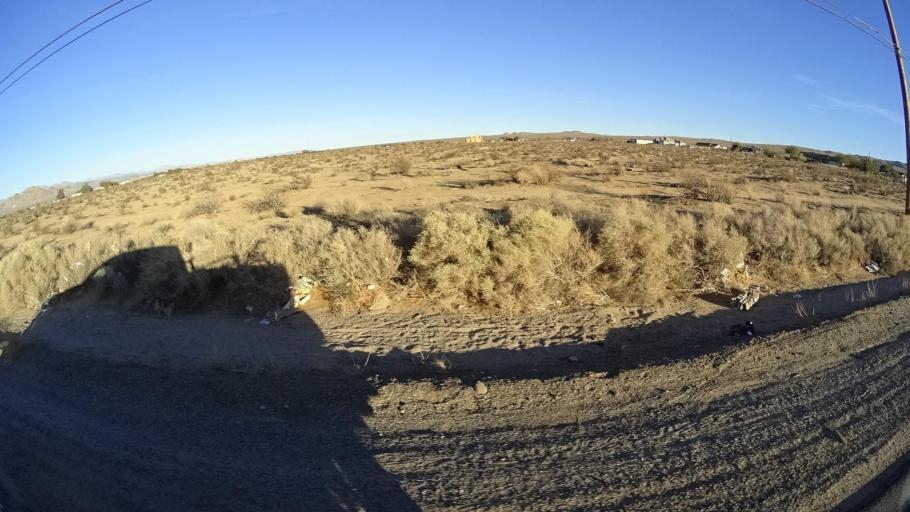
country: US
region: California
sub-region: Kern County
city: Ridgecrest
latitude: 35.6021
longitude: -117.6526
